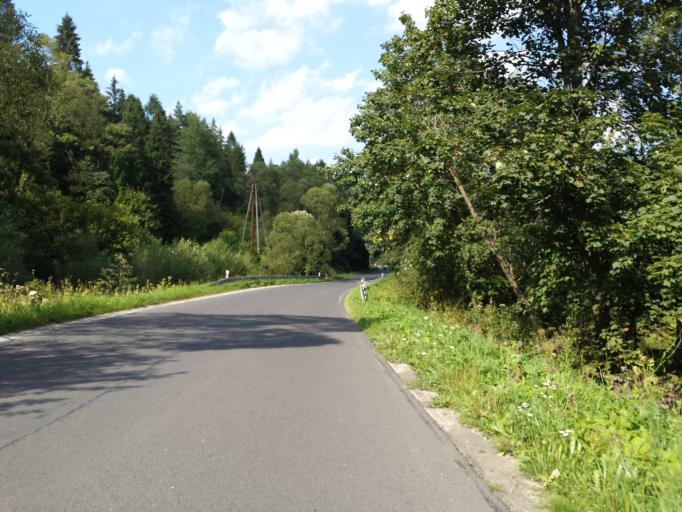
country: PL
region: Subcarpathian Voivodeship
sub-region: Powiat leski
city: Cisna
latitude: 49.2066
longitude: 22.3632
